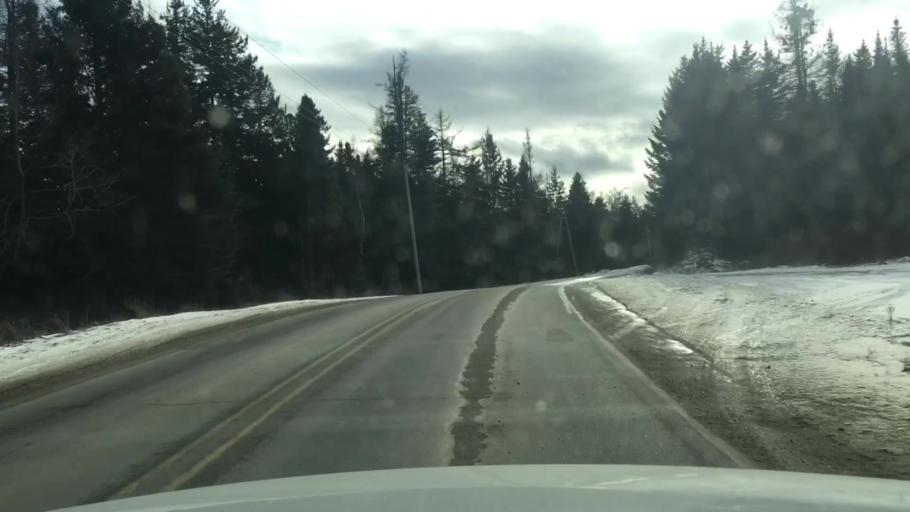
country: US
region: Maine
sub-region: Washington County
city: Jonesport
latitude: 44.6338
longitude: -67.5938
